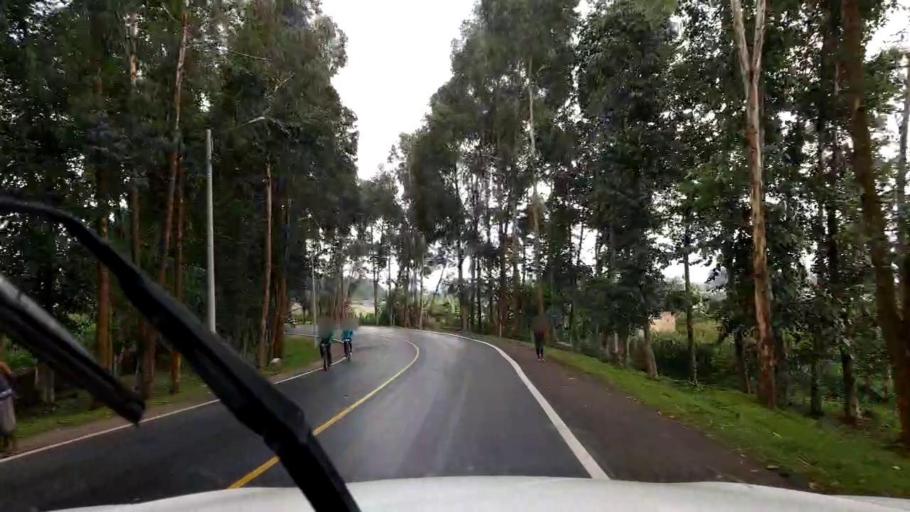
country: RW
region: Western Province
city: Gisenyi
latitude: -1.6754
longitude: 29.3563
